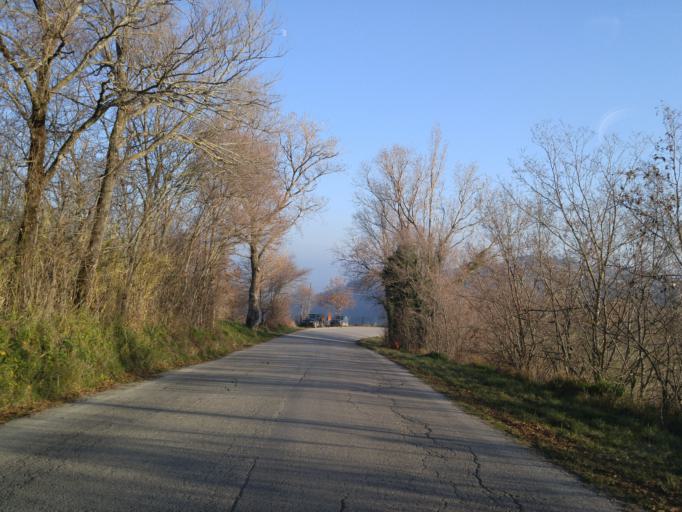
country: IT
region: The Marches
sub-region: Provincia di Pesaro e Urbino
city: Mombaroccio
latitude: 43.7782
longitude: 12.8518
